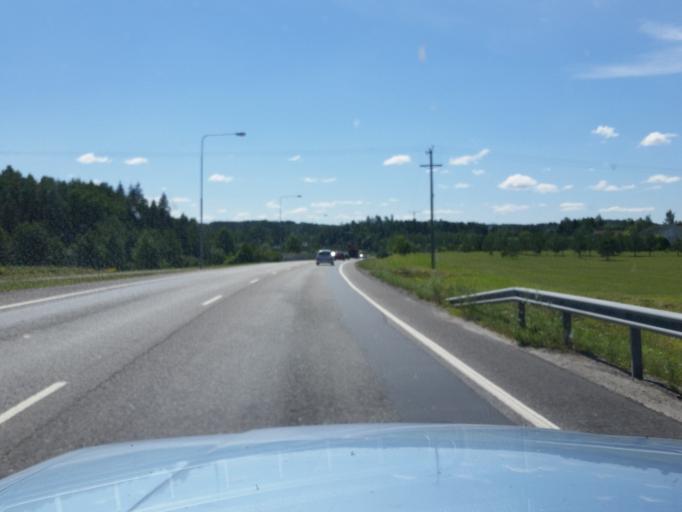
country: FI
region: Varsinais-Suomi
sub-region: Turku
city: Kaarina
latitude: 60.4050
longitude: 22.3878
